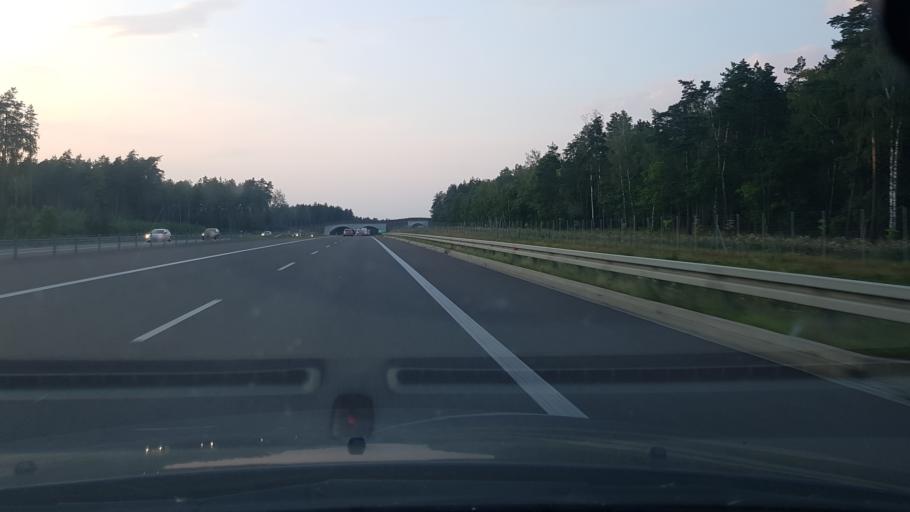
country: PL
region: Masovian Voivodeship
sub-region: Powiat mlawski
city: Wieczfnia Koscielna
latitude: 53.2472
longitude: 20.4243
